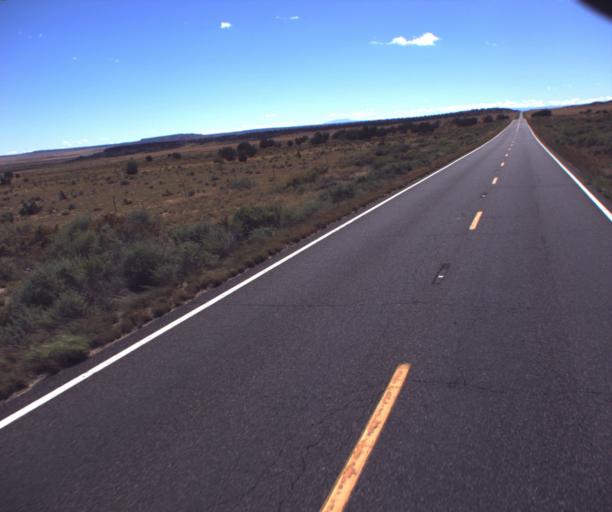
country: US
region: Arizona
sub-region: Apache County
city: Saint Johns
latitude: 34.7769
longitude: -109.2393
